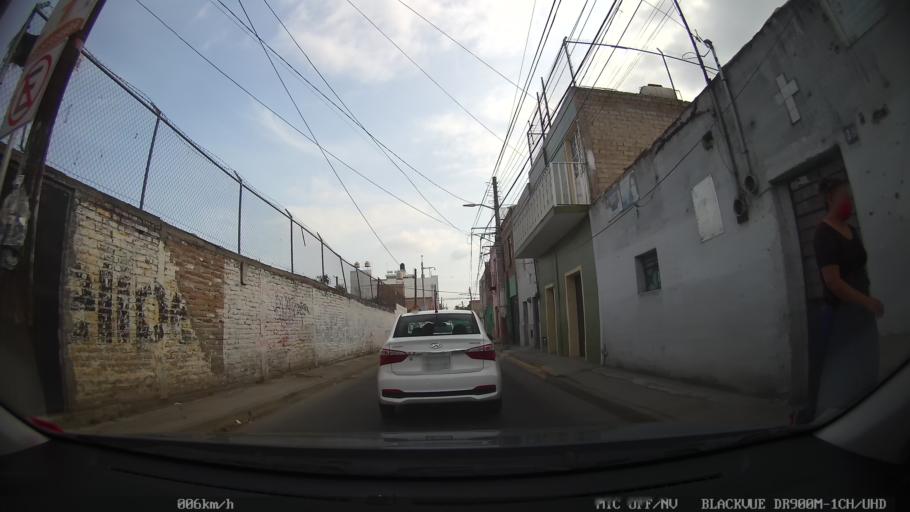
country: MX
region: Jalisco
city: Tonala
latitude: 20.6232
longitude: -103.2369
